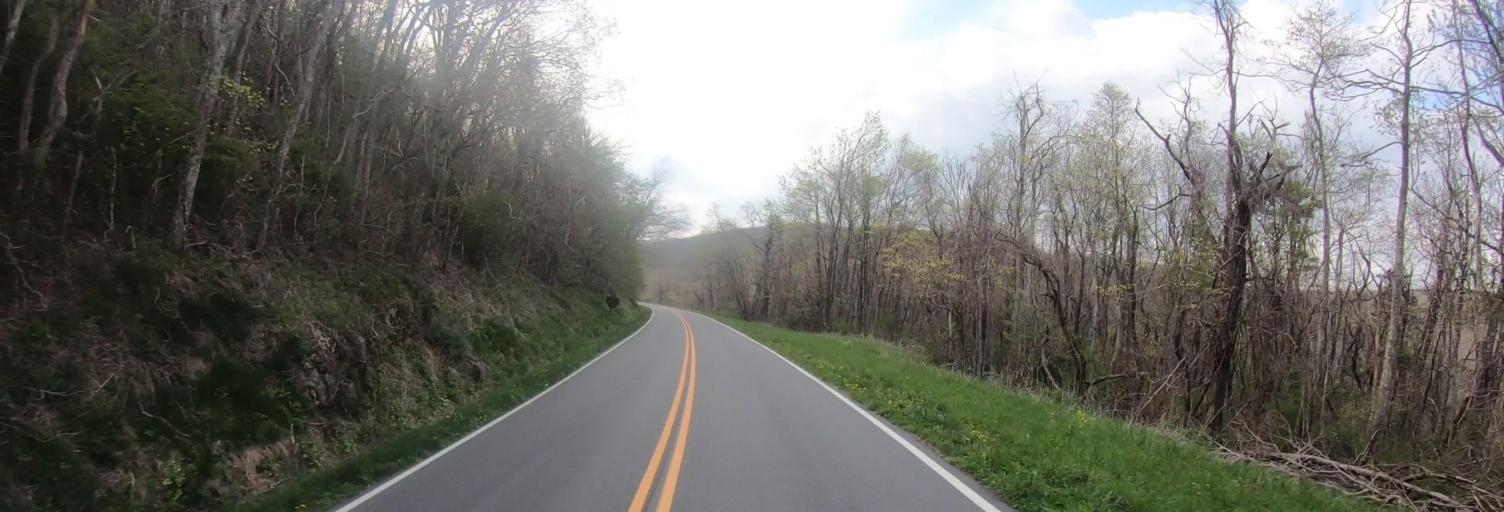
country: US
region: Virginia
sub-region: Augusta County
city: Dooms
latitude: 38.0700
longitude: -78.7899
